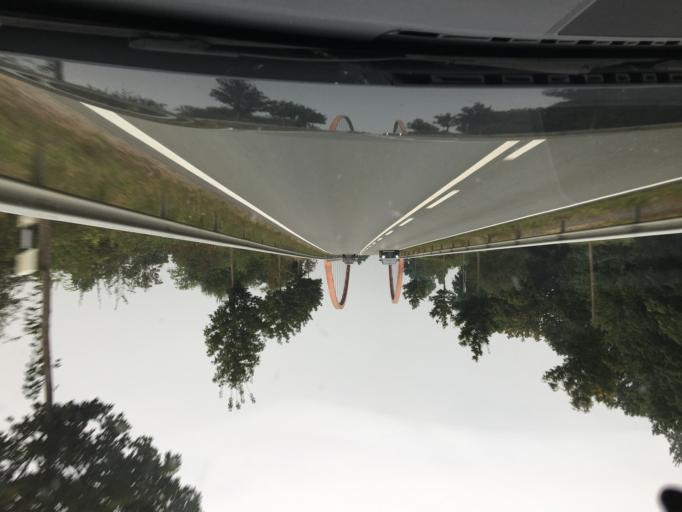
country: DE
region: North Rhine-Westphalia
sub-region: Regierungsbezirk Munster
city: Ladbergen
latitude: 52.1150
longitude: 7.7116
